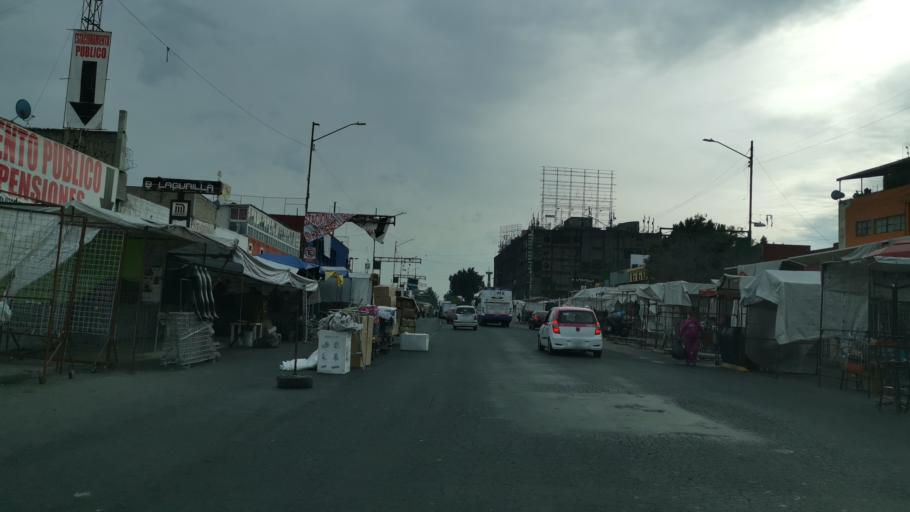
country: MX
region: Mexico City
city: Cuauhtemoc
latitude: 19.4434
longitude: -99.1323
